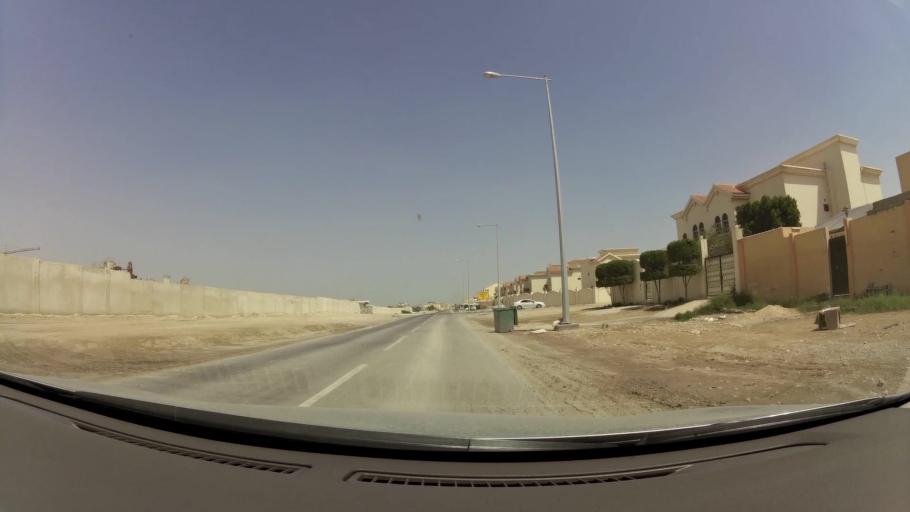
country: QA
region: Baladiyat Umm Salal
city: Umm Salal Muhammad
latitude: 25.3792
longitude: 51.4493
